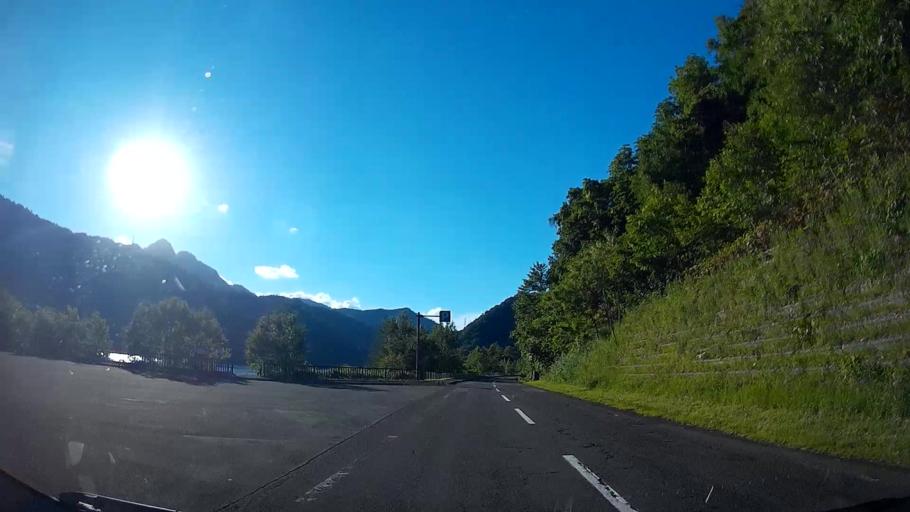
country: JP
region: Hokkaido
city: Sapporo
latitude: 43.0003
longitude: 141.1516
